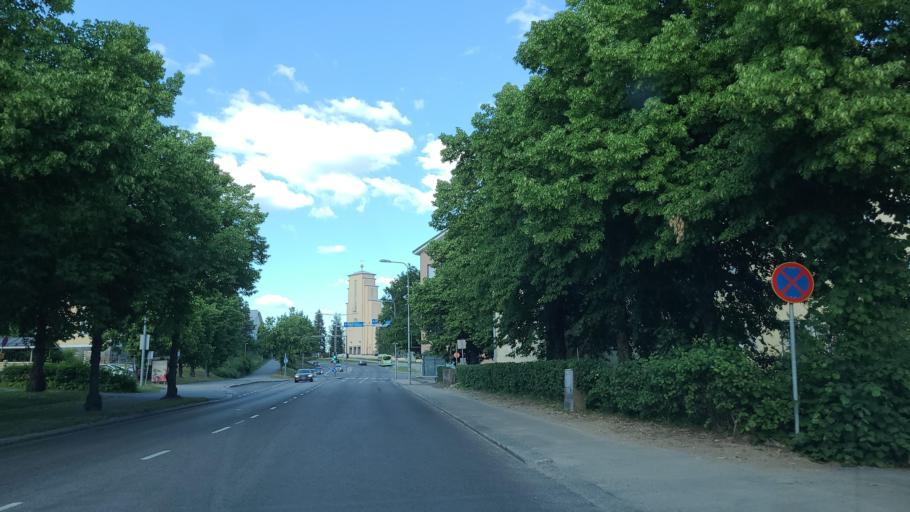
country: FI
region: Central Finland
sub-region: Jyvaeskylae
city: Jyvaeskylae
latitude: 62.2518
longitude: 25.7471
